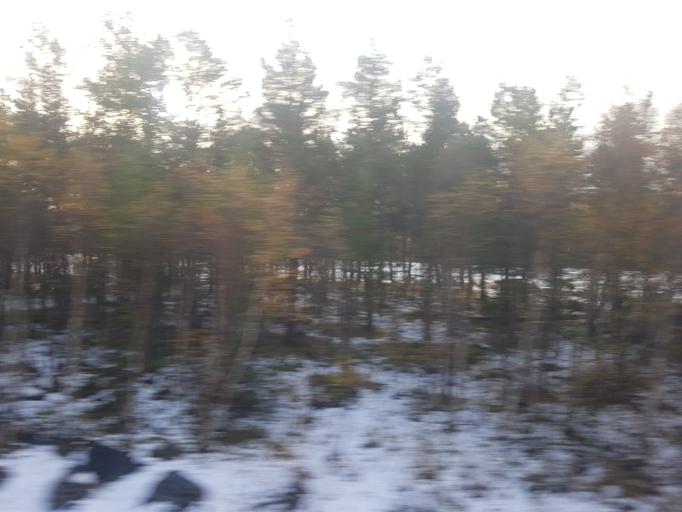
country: NO
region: Sor-Trondelag
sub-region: Oppdal
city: Oppdal
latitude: 62.6390
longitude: 9.8081
